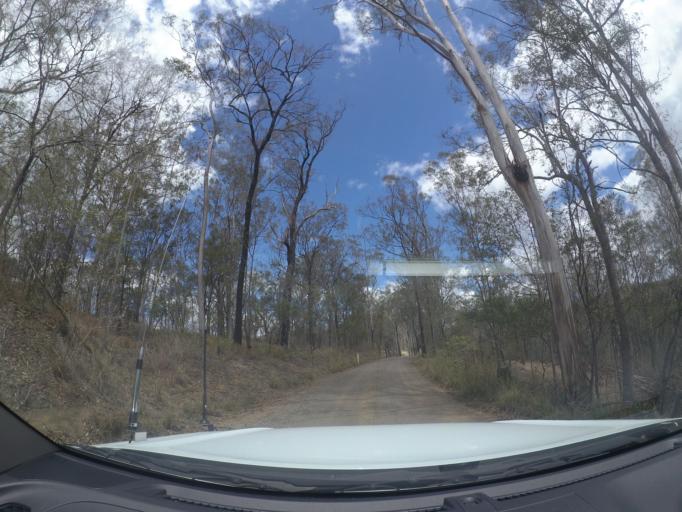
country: AU
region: Queensland
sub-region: Logan
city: Cedar Vale
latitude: -27.8895
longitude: 153.0438
